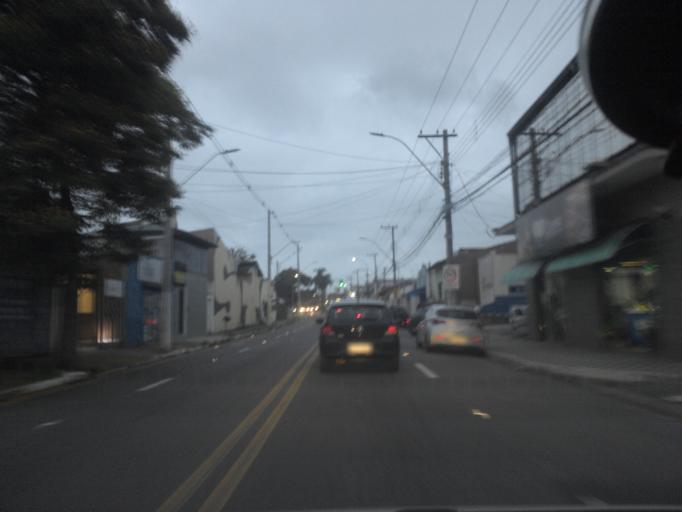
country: BR
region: Sao Paulo
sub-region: Taubate
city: Taubate
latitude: -23.0222
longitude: -45.5445
